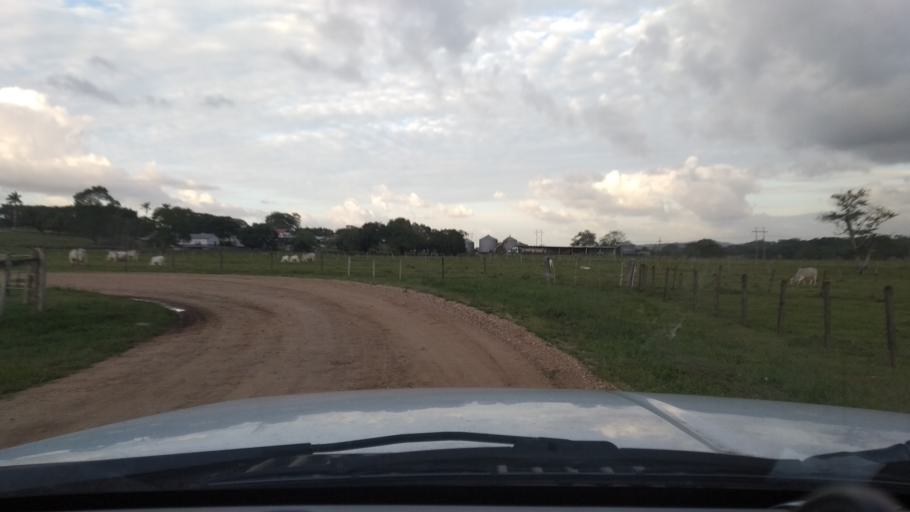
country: BZ
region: Cayo
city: San Ignacio
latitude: 17.2242
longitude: -88.9929
